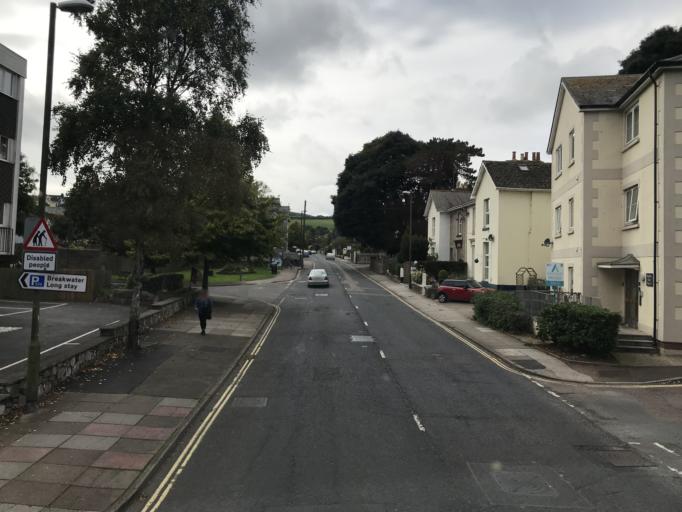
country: GB
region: England
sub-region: Borough of Torbay
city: Brixham
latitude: 50.3924
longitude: -3.5222
